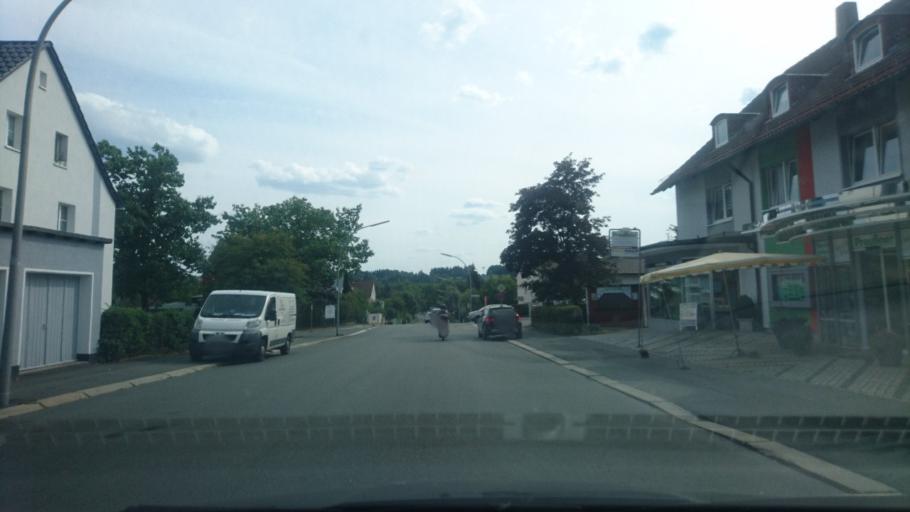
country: DE
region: Bavaria
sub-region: Upper Franconia
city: Hof
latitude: 50.3150
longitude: 11.9014
